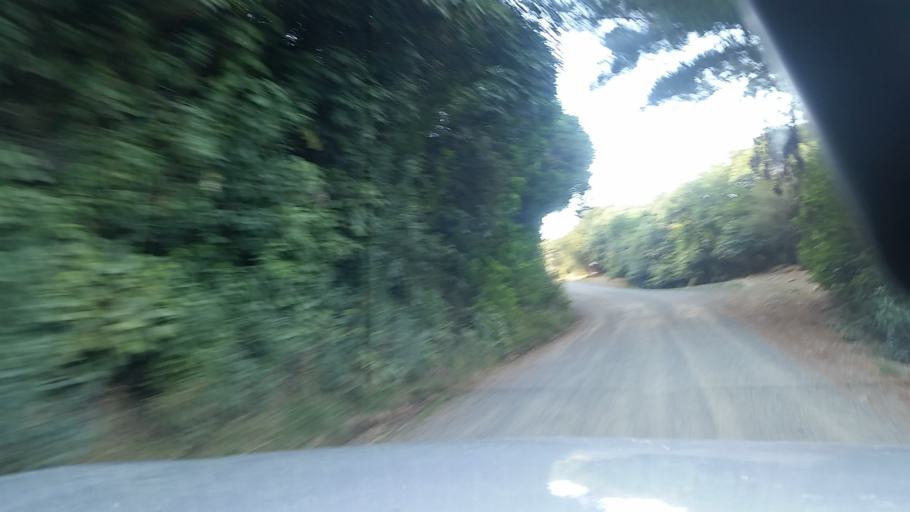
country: NZ
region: Marlborough
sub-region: Marlborough District
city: Picton
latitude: -41.2972
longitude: 174.1214
